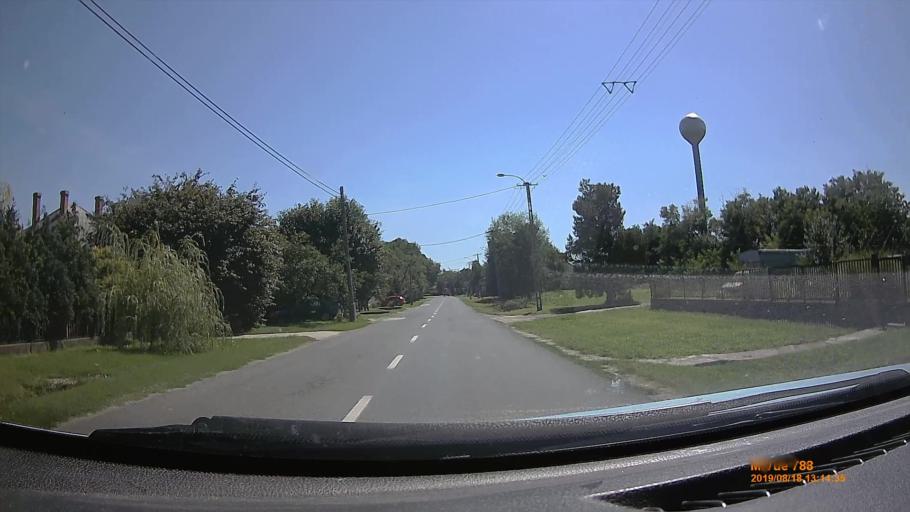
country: HU
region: Fejer
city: Sarbogard
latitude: 46.8742
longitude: 18.5403
